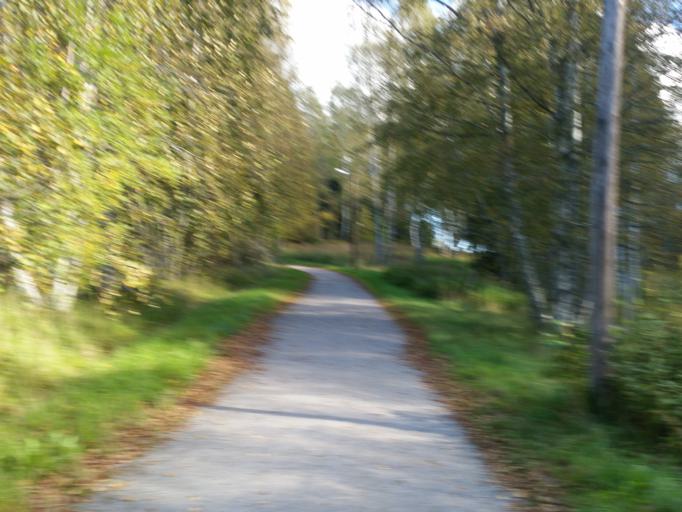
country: SE
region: Stockholm
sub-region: Tyreso Kommun
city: Bollmora
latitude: 59.1685
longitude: 18.2271
